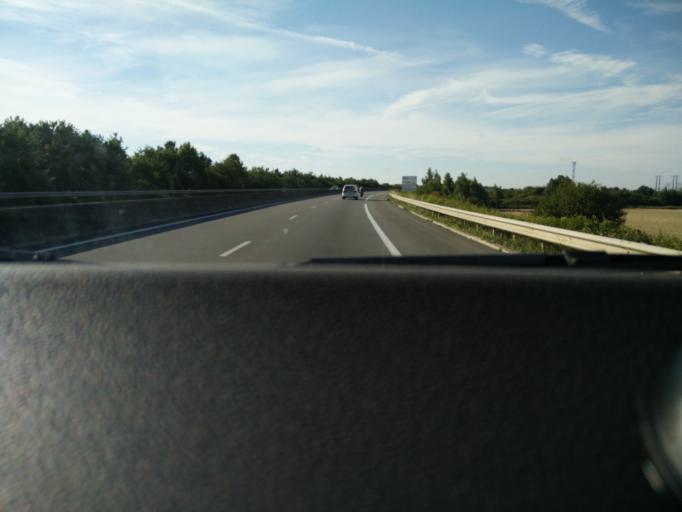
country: FR
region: Nord-Pas-de-Calais
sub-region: Departement du Nord
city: Somain
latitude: 50.3507
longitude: 3.2646
